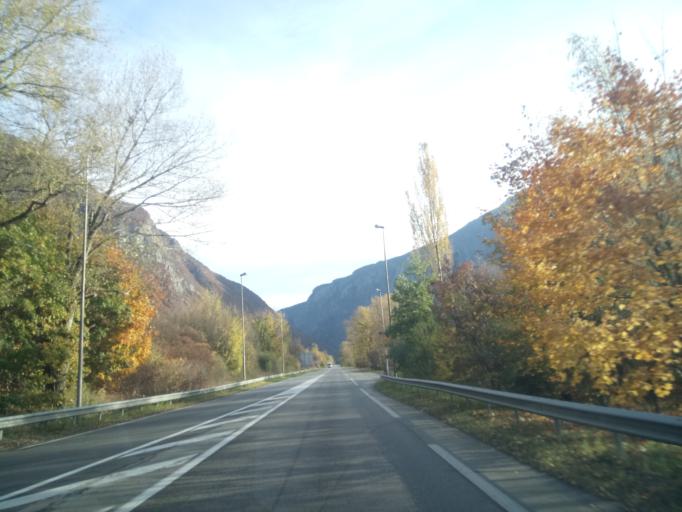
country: FR
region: Rhone-Alpes
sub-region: Departement de la Savoie
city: La Chambre
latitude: 45.3474
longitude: 6.3066
